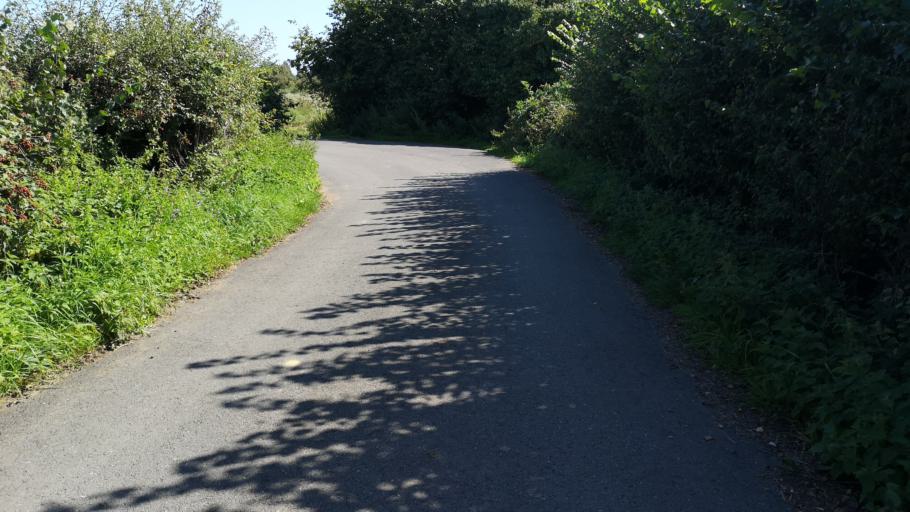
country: GB
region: England
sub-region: Isle of Wight
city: Brading
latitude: 50.6678
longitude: -1.1533
